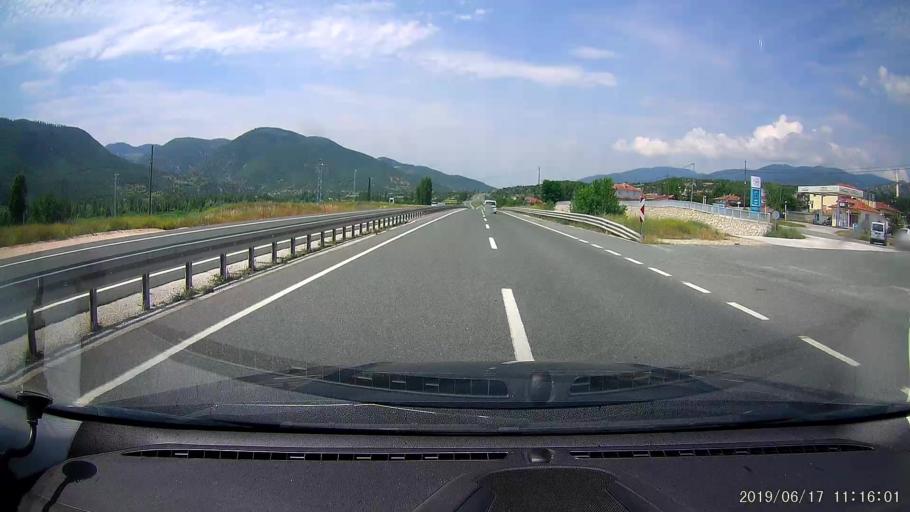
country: TR
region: Kastamonu
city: Tosya
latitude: 40.9492
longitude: 33.9090
